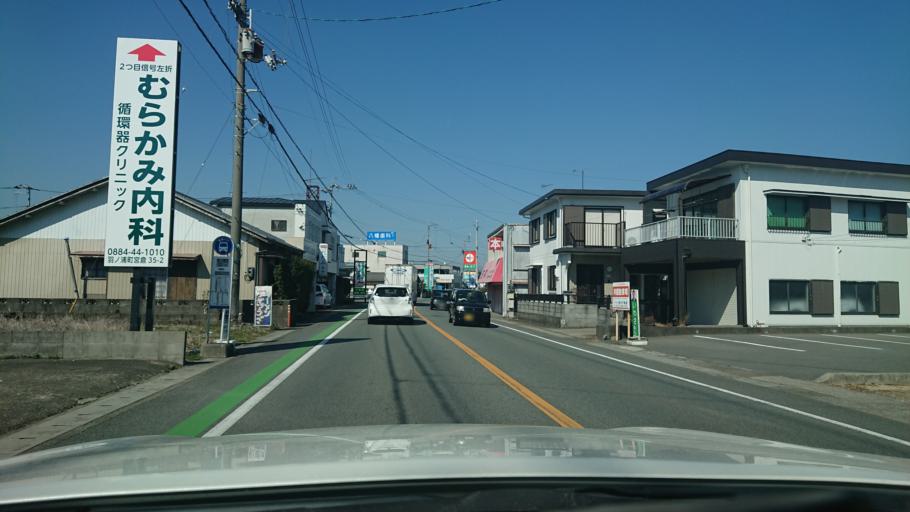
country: JP
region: Tokushima
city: Komatsushimacho
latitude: 33.9625
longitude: 134.6218
